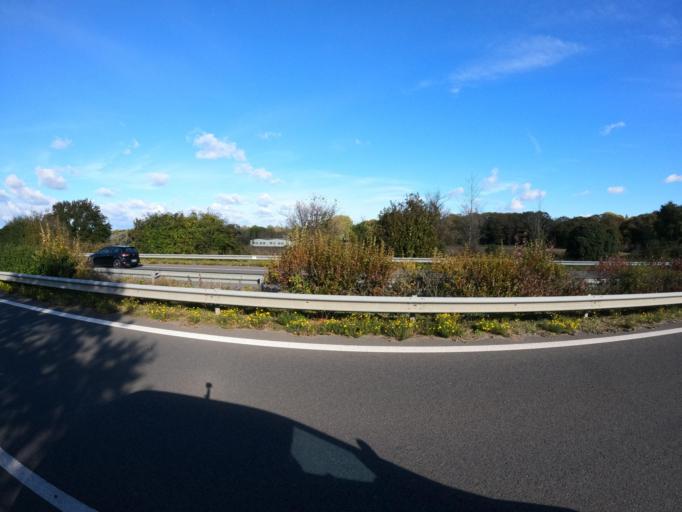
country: FR
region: Pays de la Loire
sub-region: Departement de la Loire-Atlantique
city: Pornichet
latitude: 47.2896
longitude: -2.3305
